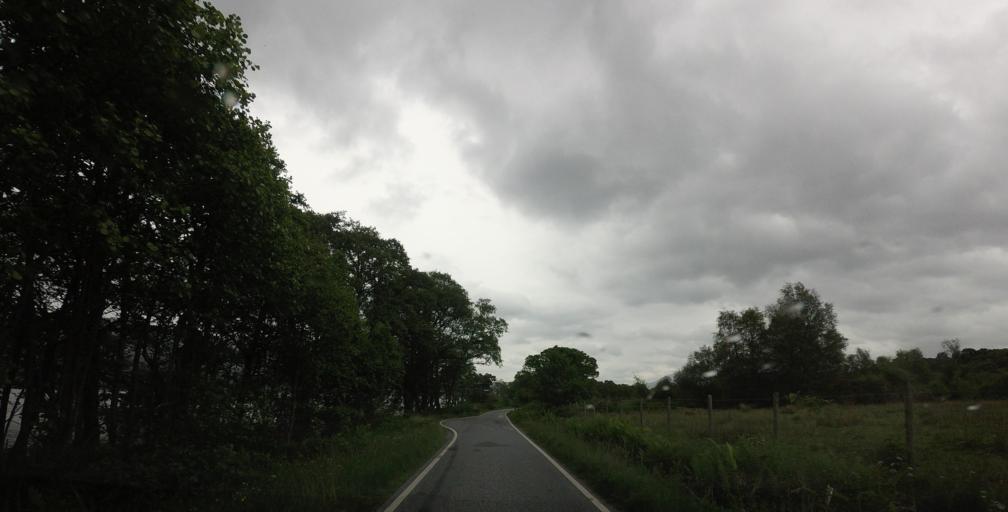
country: GB
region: Scotland
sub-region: Highland
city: Fort William
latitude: 56.8423
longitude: -5.2415
